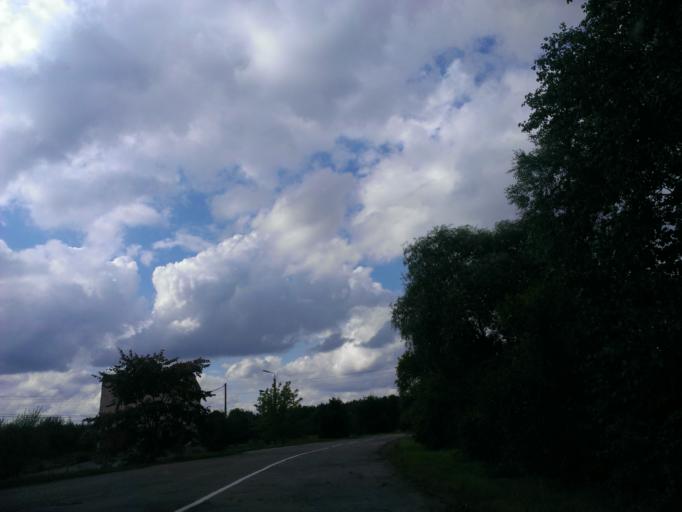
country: LV
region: Garkalne
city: Garkalne
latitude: 56.9649
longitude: 24.5064
